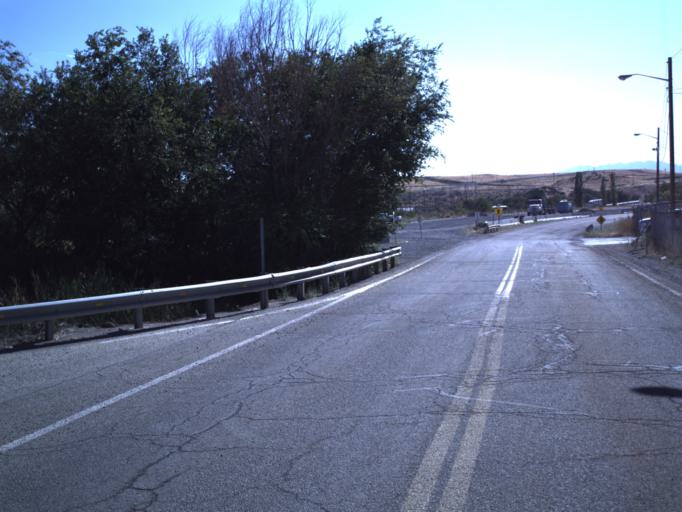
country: US
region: Utah
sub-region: Salt Lake County
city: Magna
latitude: 40.7271
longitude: -112.1697
